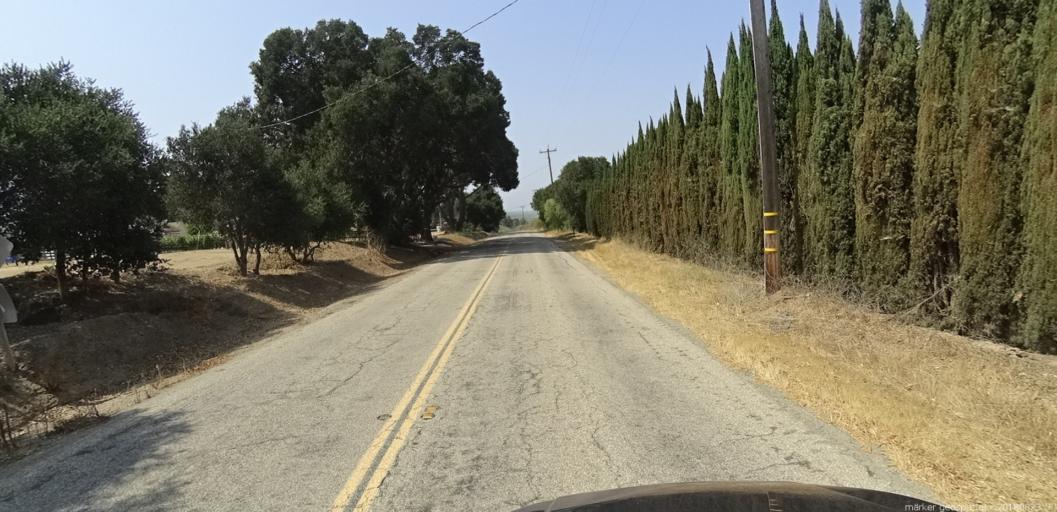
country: US
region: California
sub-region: Monterey County
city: Gonzales
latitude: 36.4456
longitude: -121.4320
